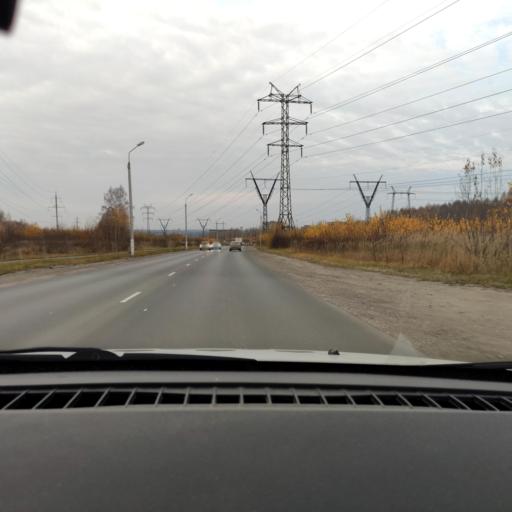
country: RU
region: Perm
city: Perm
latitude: 58.0978
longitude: 56.3954
